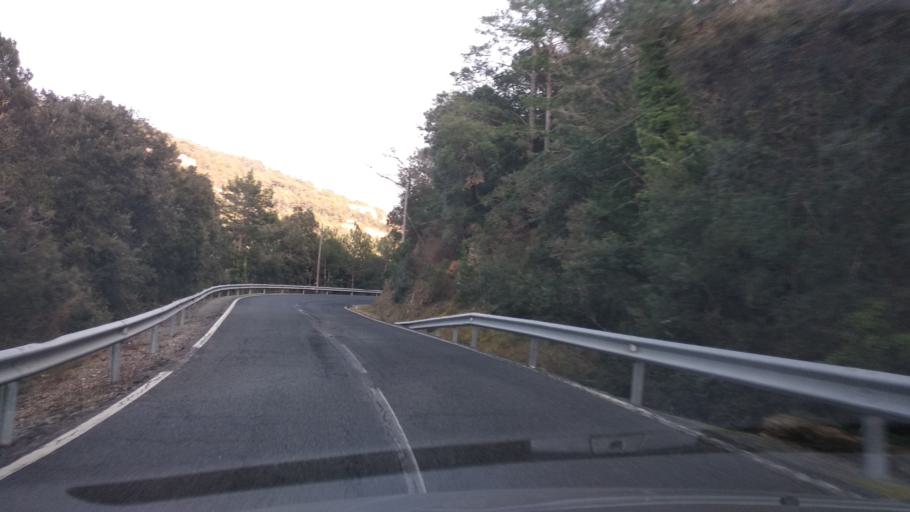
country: ES
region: Catalonia
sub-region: Provincia de Tarragona
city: Alforja
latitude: 41.2227
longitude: 0.9289
